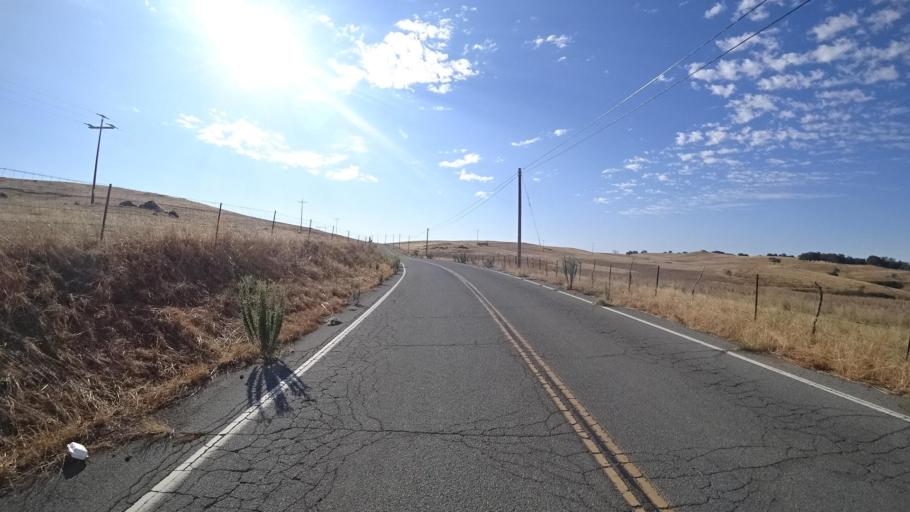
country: US
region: California
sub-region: San Diego County
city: Julian
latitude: 33.1662
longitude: -116.7378
